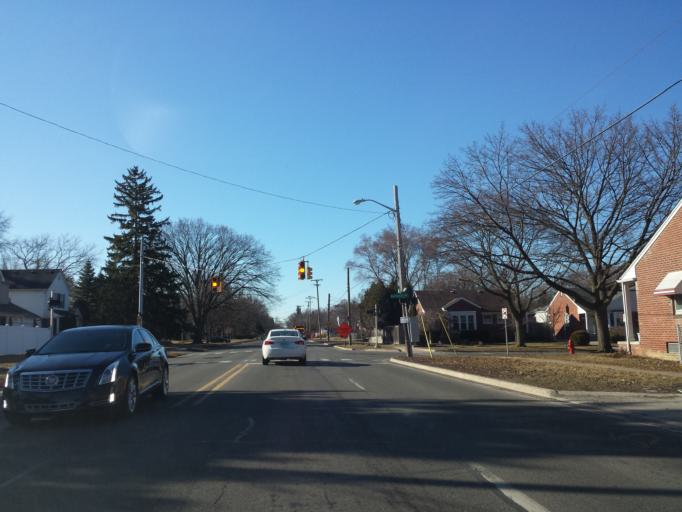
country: US
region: Michigan
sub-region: Oakland County
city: Clawson
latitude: 42.5267
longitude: -83.1460
